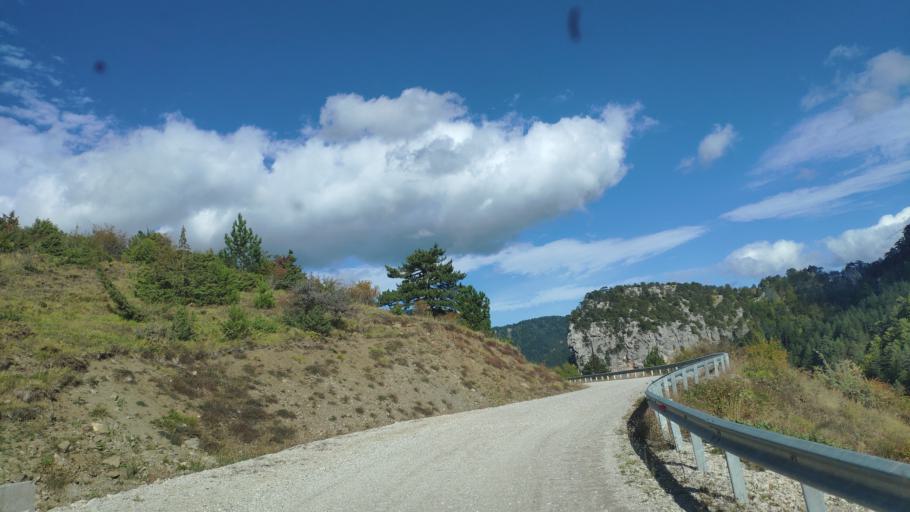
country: AL
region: Korce
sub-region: Rrethi i Devollit
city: Miras
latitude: 40.4037
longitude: 20.8546
